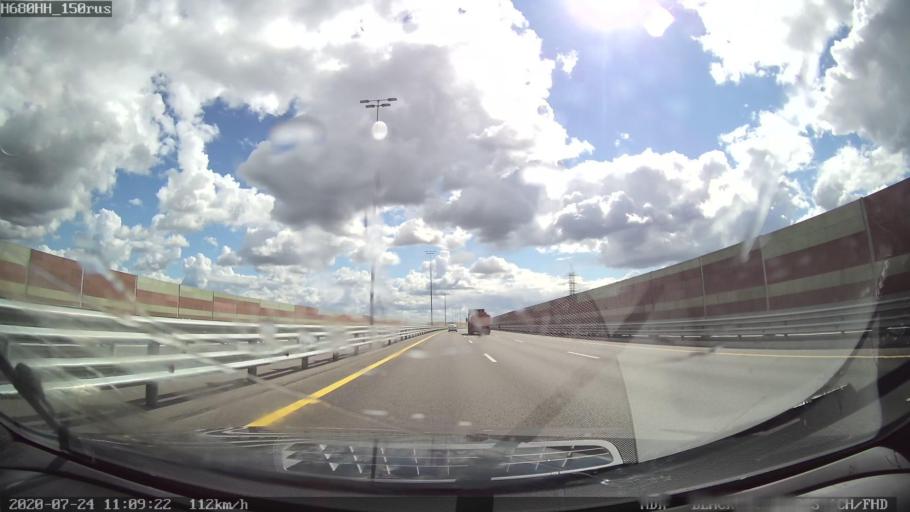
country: RU
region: St.-Petersburg
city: Tyarlevo
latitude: 59.7495
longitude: 30.4723
